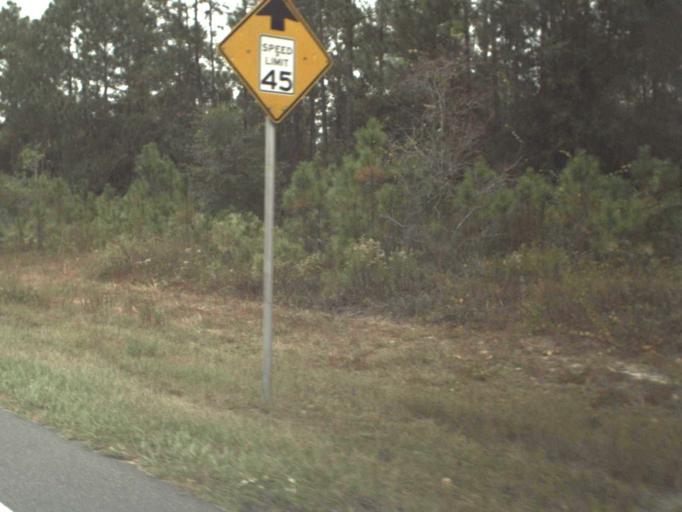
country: US
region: Florida
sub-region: Wakulla County
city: Crawfordville
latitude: 30.2552
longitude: -84.3622
